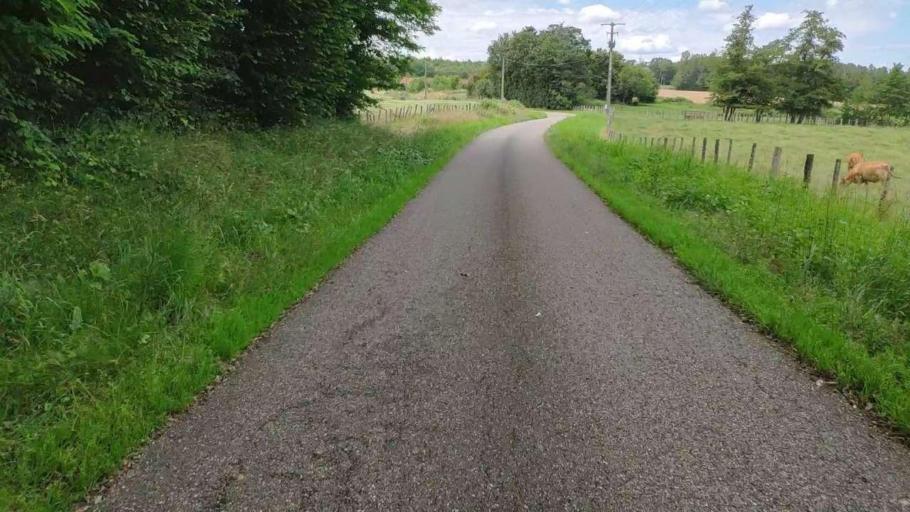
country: FR
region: Franche-Comte
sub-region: Departement du Jura
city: Chaussin
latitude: 46.8860
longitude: 5.4483
